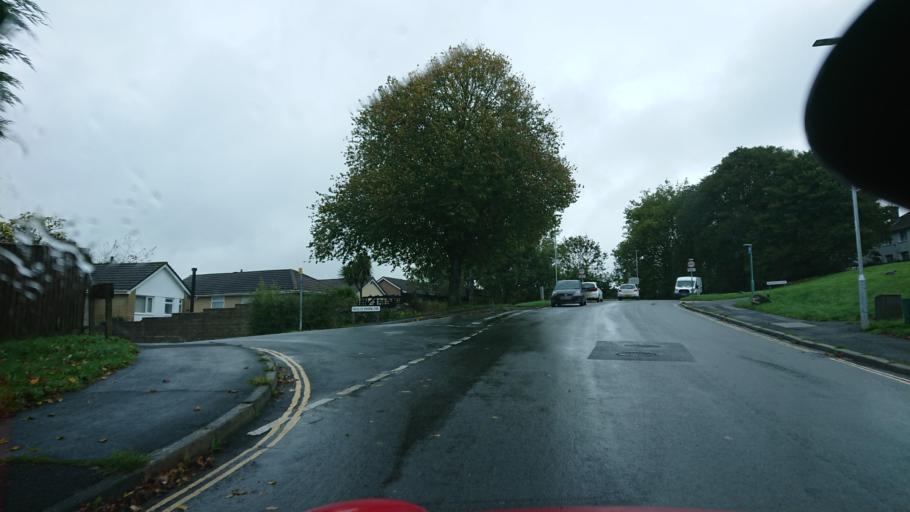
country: GB
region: England
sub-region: Plymouth
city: Plymouth
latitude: 50.4220
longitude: -4.1646
